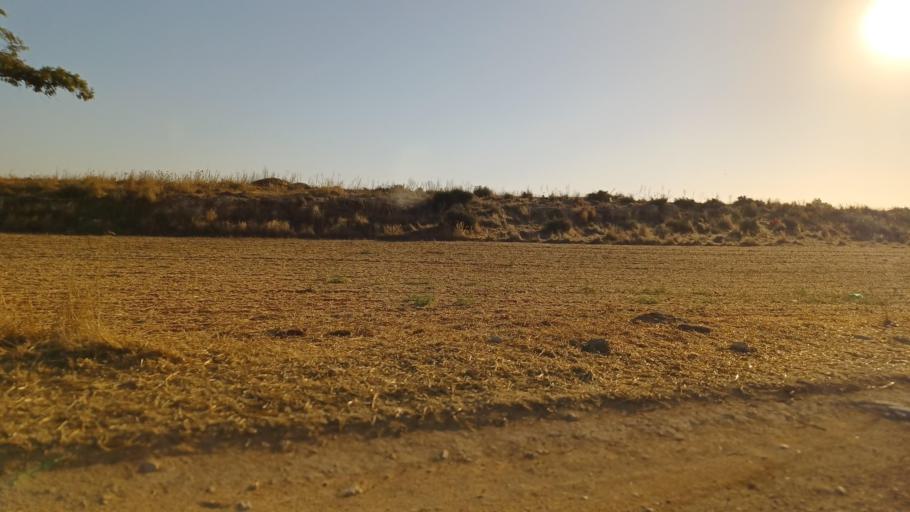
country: CY
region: Ammochostos
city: Achna
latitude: 35.0397
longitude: 33.7956
